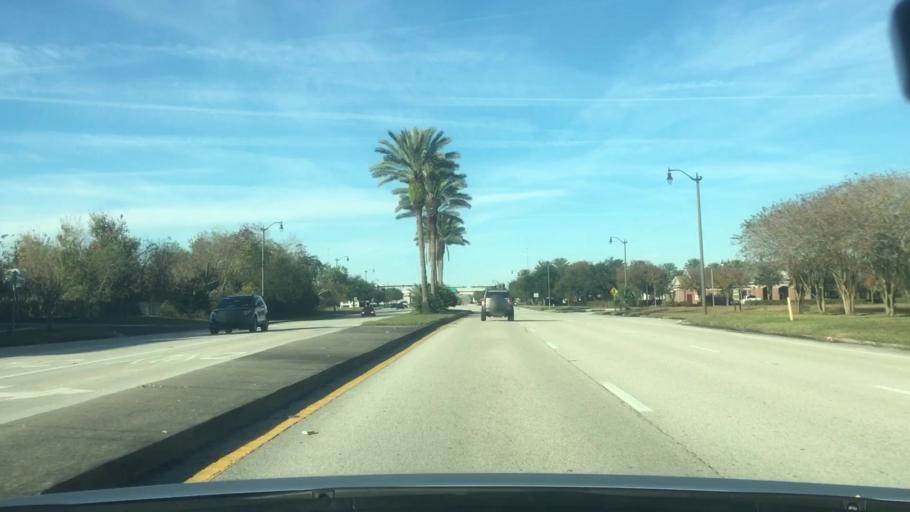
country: US
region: Florida
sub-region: Duval County
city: Jacksonville
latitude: 30.3381
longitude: -81.5460
